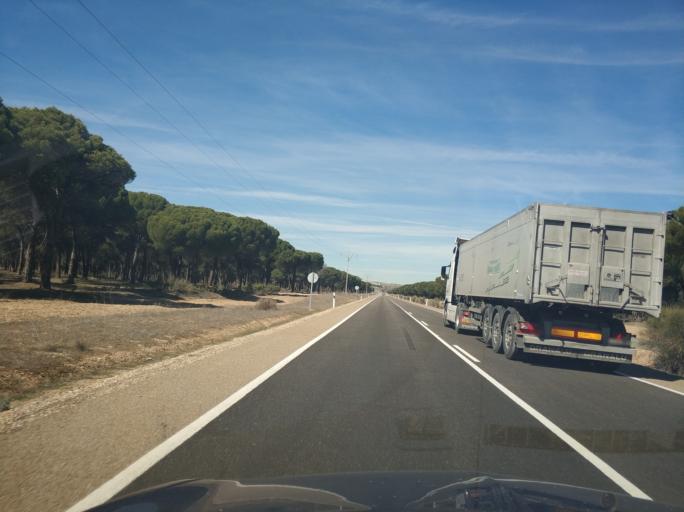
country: ES
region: Castille and Leon
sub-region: Provincia de Valladolid
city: Simancas
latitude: 41.5688
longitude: -4.8035
